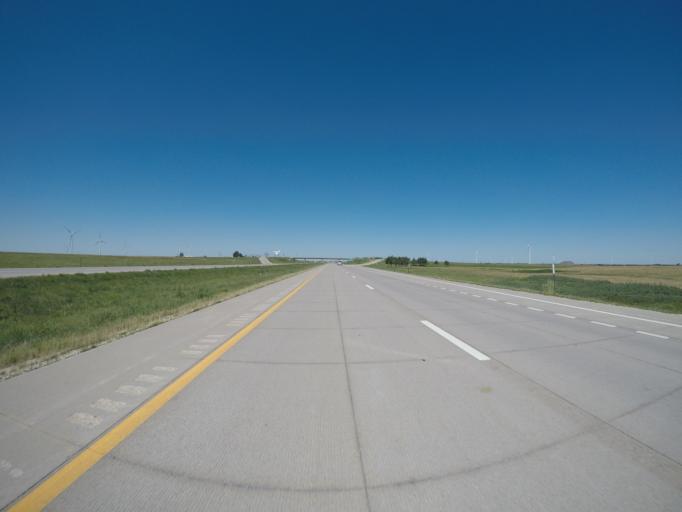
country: US
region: Kansas
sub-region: Ellsworth County
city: Ellsworth
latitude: 38.8495
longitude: -98.2772
